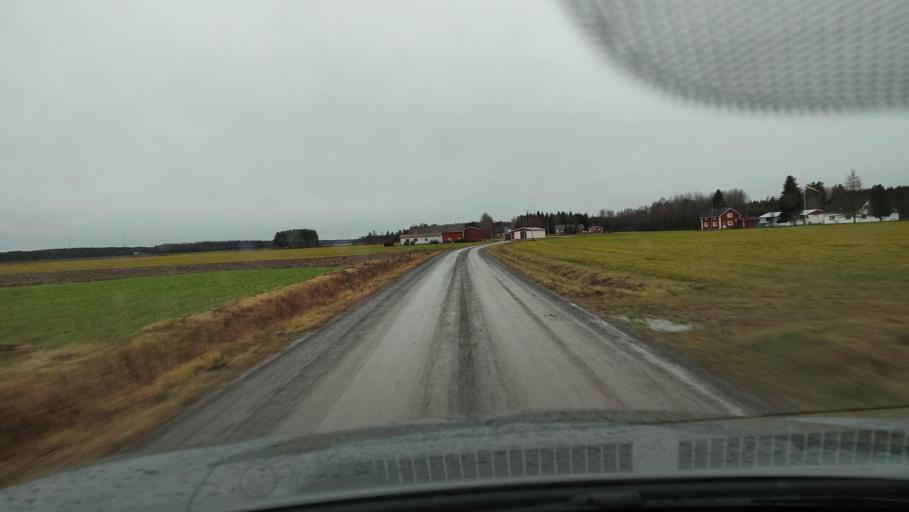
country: FI
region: Southern Ostrobothnia
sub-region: Suupohja
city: Karijoki
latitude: 62.2411
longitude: 21.5515
